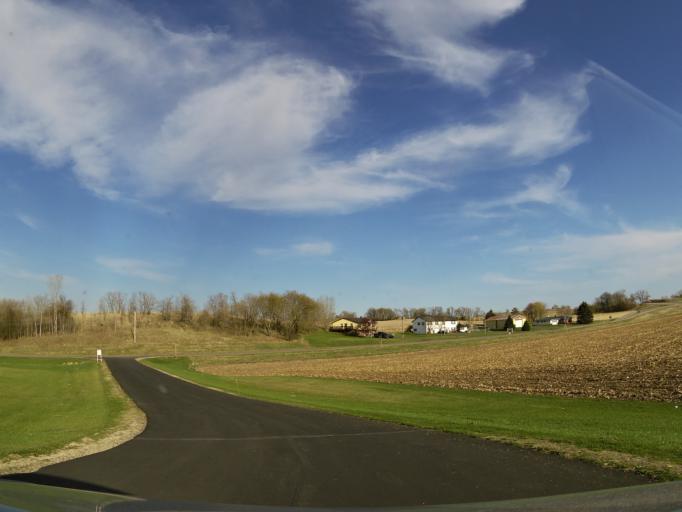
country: US
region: Wisconsin
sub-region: Pierce County
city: River Falls
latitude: 44.7452
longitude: -92.6410
